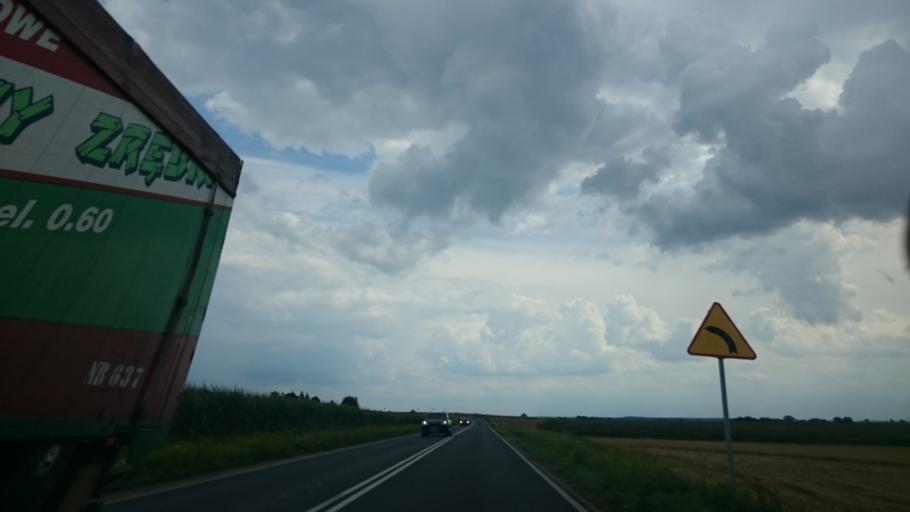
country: PL
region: Pomeranian Voivodeship
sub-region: Powiat chojnicki
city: Chojnice
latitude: 53.6650
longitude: 17.6678
